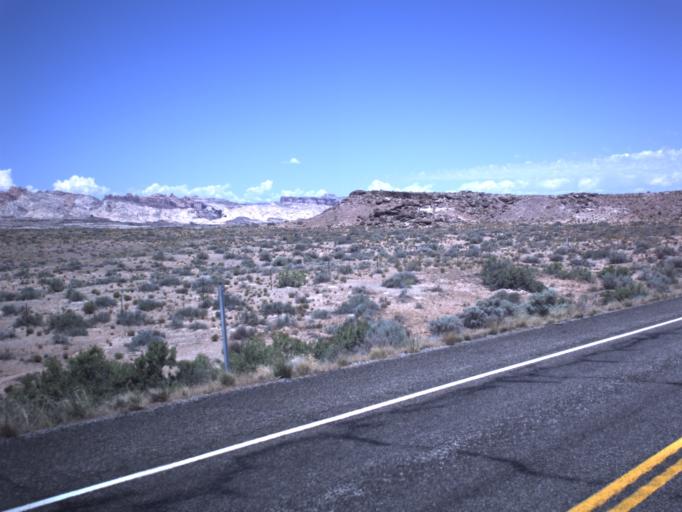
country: US
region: Utah
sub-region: Carbon County
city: East Carbon City
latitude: 38.8872
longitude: -110.3586
